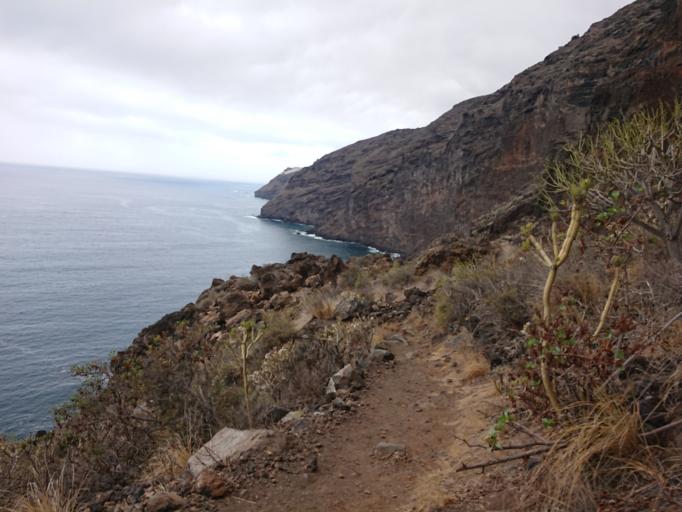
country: ES
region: Canary Islands
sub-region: Provincia de Santa Cruz de Tenerife
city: Tijarafe
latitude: 28.7190
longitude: -17.9783
